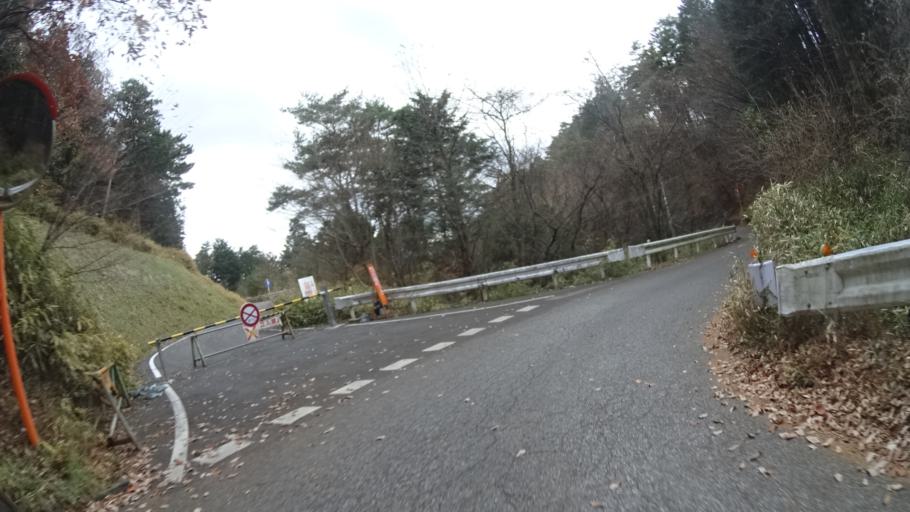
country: JP
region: Gunma
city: Omamacho-omama
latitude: 36.5031
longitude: 139.1838
